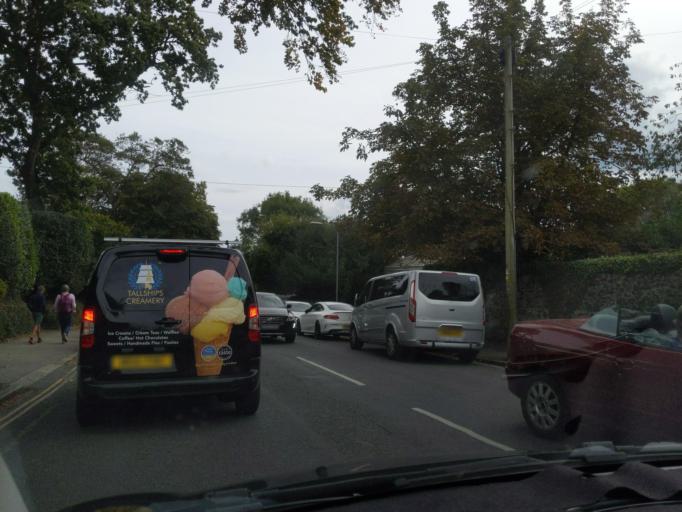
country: GB
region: England
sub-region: Cornwall
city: St Austell
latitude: 50.3355
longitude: -4.7617
